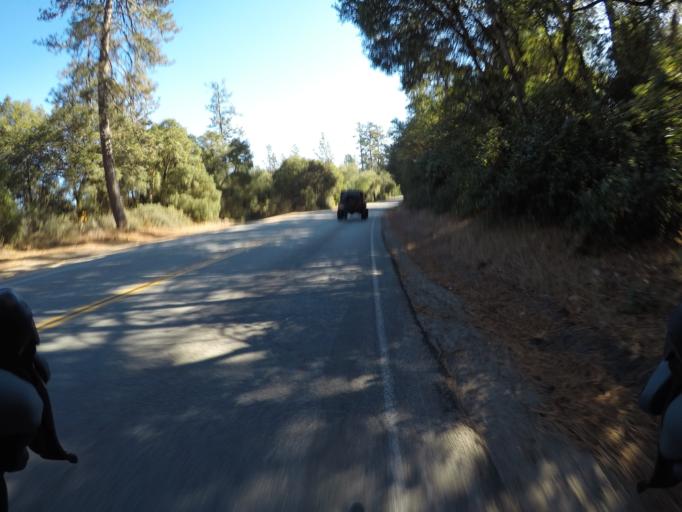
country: US
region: California
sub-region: Santa Cruz County
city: Mount Hermon
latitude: 37.0413
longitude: -122.0458
